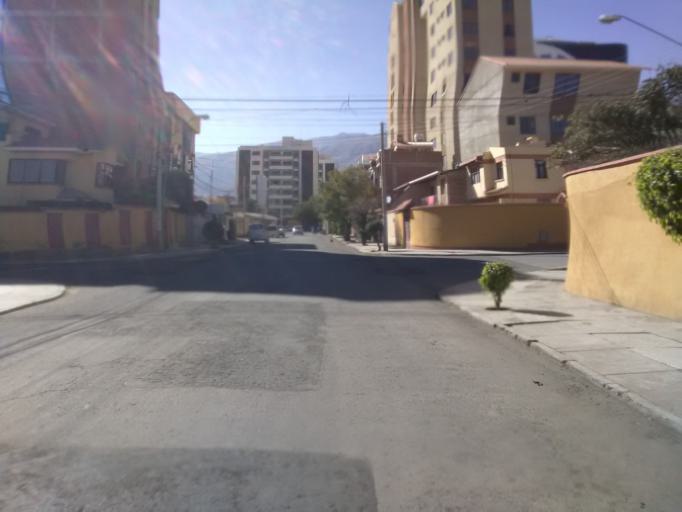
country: BO
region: Cochabamba
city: Cochabamba
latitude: -17.3736
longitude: -66.1644
